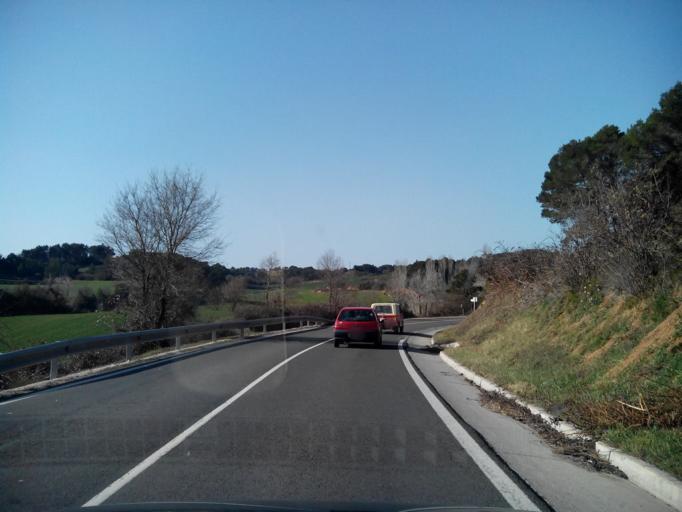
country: ES
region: Catalonia
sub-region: Provincia de Tarragona
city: Conesa
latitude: 41.4964
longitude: 1.3349
